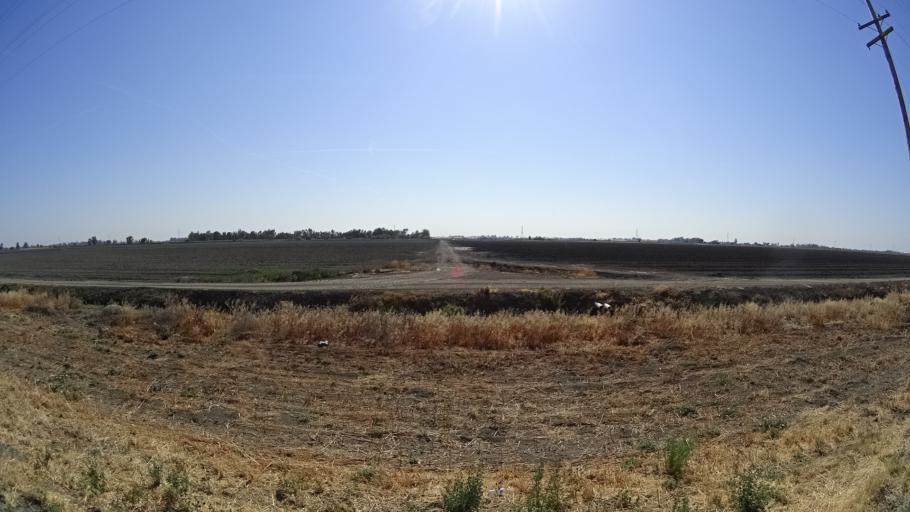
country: US
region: California
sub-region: Kings County
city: Lemoore Station
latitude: 36.3499
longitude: -119.9053
